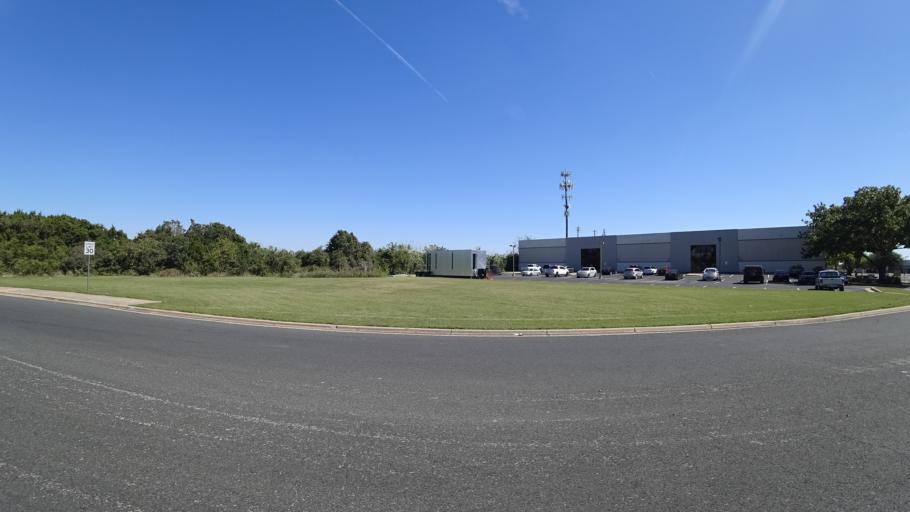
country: US
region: Texas
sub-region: Travis County
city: Austin
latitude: 30.2777
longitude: -97.6716
